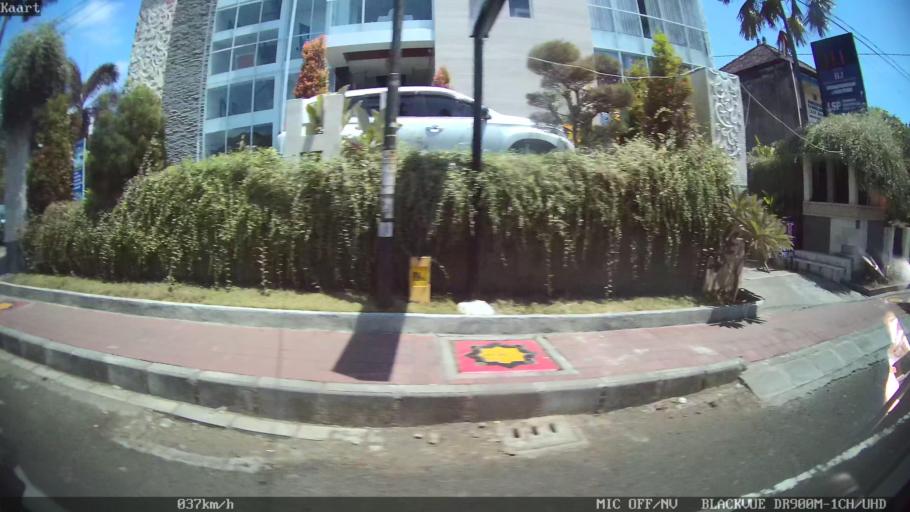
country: ID
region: Bali
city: Sukasada
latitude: -8.1447
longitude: 115.1046
